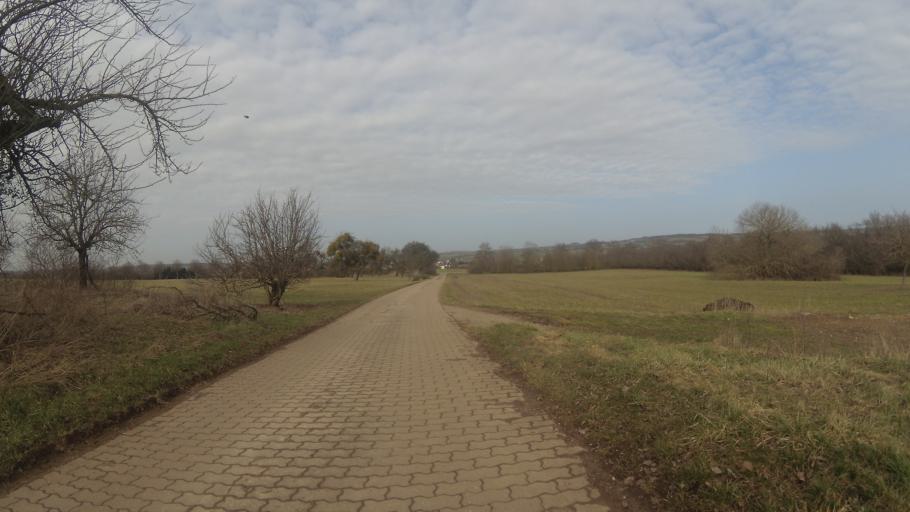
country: FR
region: Lorraine
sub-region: Departement de la Moselle
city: Merten
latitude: 49.2873
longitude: 6.6610
